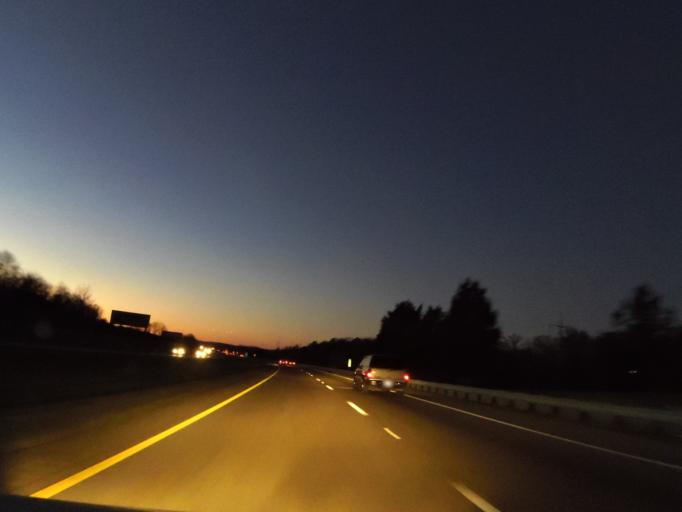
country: US
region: Tennessee
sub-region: Jefferson County
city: White Pine
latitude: 36.0237
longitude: -83.3014
